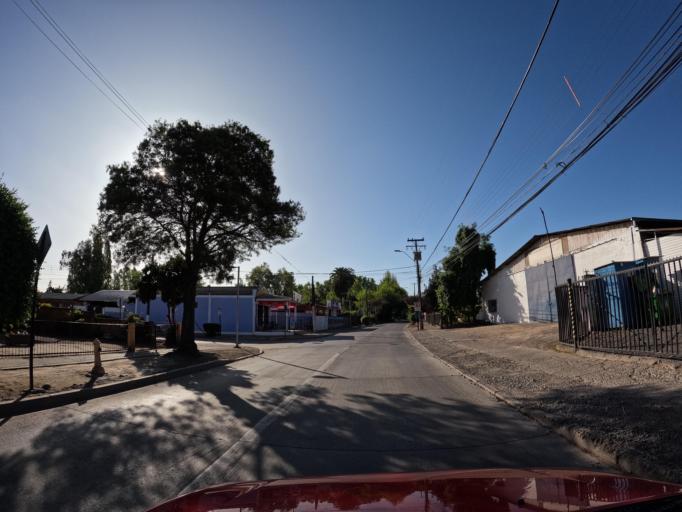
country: CL
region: O'Higgins
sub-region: Provincia de Colchagua
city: Santa Cruz
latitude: -34.7333
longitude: -71.2693
